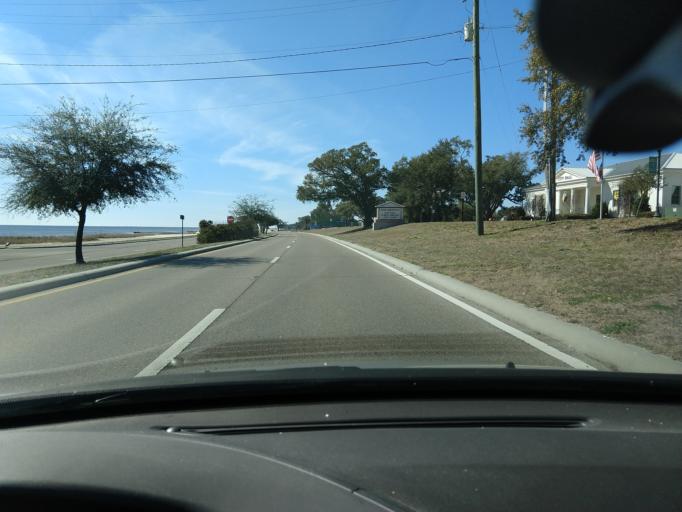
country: US
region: Mississippi
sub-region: Harrison County
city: Pass Christian
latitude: 30.3133
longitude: -89.2495
